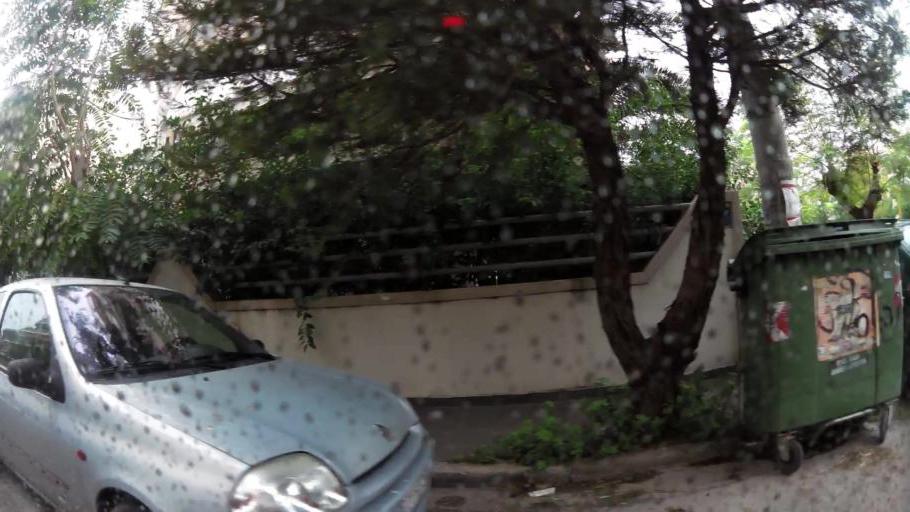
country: GR
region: Attica
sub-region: Nomarchia Athinas
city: Peristeri
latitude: 38.0134
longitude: 23.7104
